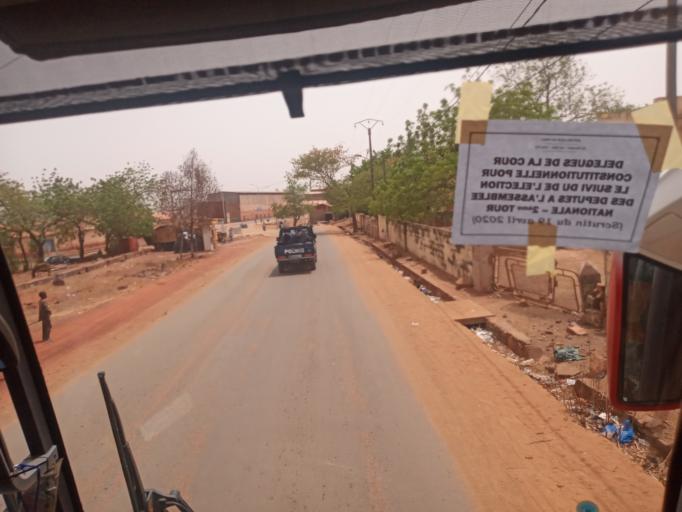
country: ML
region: Koulikoro
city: Koulikoro
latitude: 12.8561
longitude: -7.5623
